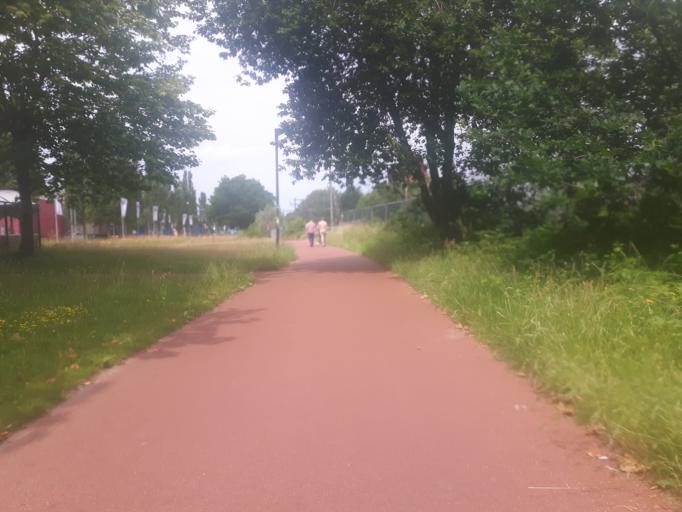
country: NL
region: Overijssel
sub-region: Gemeente Hengelo
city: Hengelo
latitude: 52.2380
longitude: 6.8375
